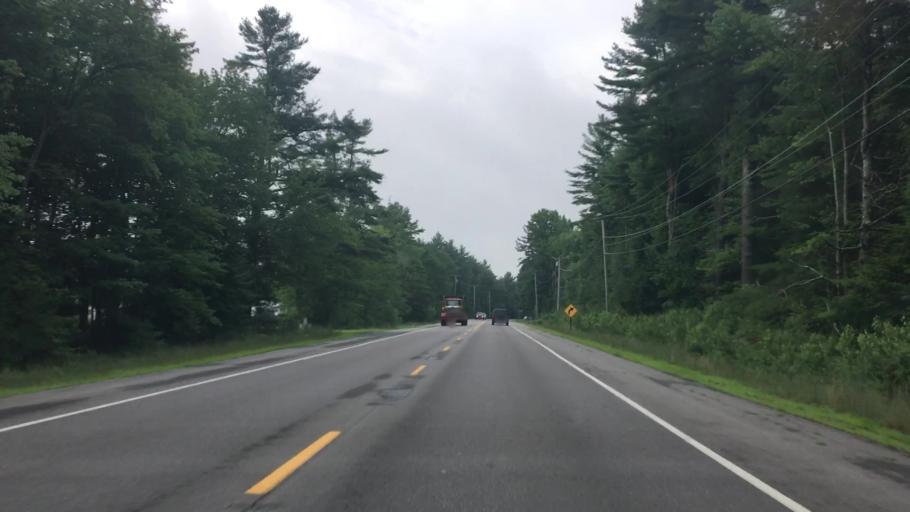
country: US
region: Maine
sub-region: York County
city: Lebanon
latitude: 43.3855
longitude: -70.8765
